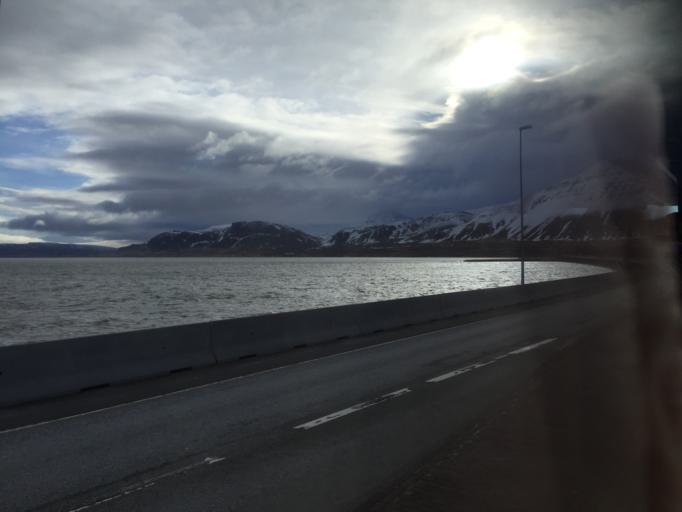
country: IS
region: West
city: Borgarnes
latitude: 64.5394
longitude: -21.9064
